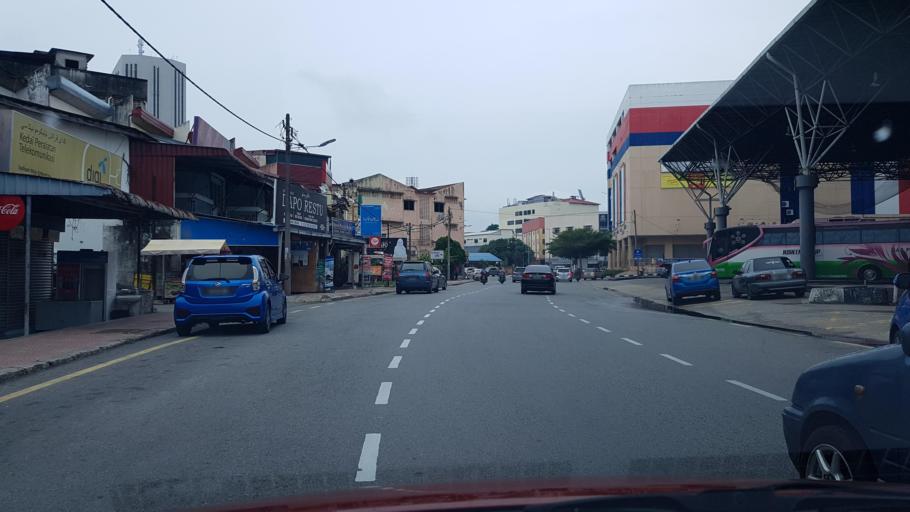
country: MY
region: Terengganu
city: Kuala Terengganu
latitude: 5.3324
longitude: 103.1375
